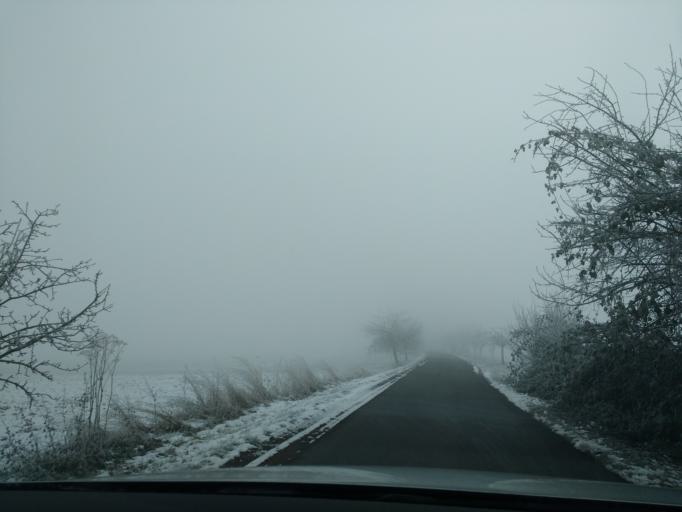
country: DE
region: Saxony-Anhalt
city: Oppin
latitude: 51.5822
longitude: 12.0006
